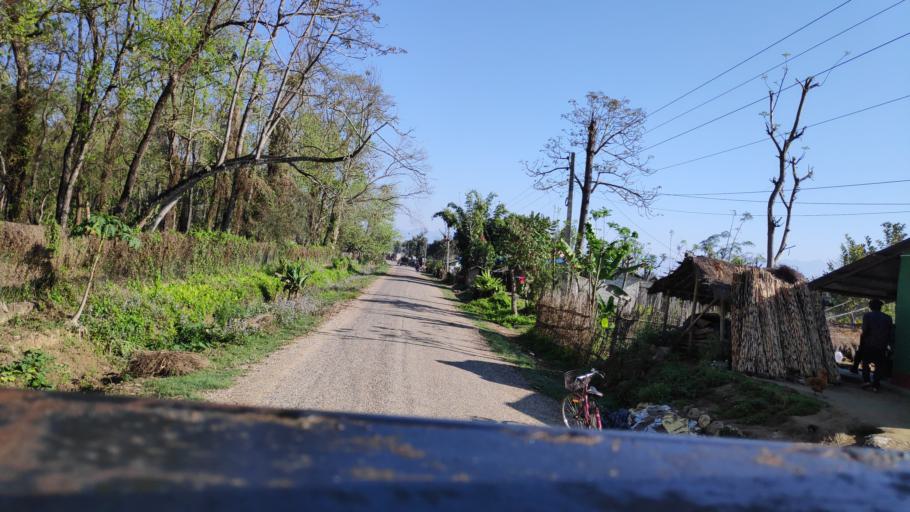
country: NP
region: Central Region
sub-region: Narayani Zone
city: Bharatpur
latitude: 27.5727
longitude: 84.5179
